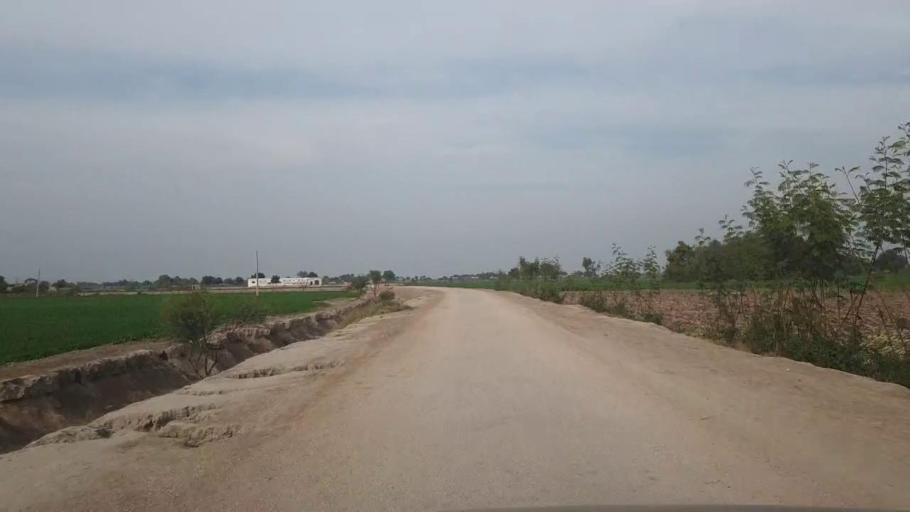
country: PK
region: Sindh
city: Shahpur Chakar
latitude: 26.1179
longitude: 68.5232
